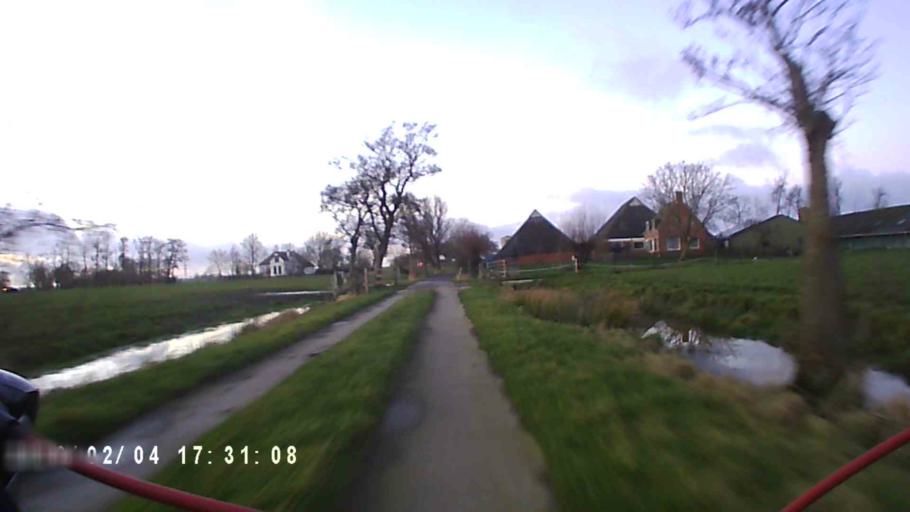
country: NL
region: Groningen
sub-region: Gemeente Zuidhorn
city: Aduard
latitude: 53.2771
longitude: 6.5001
